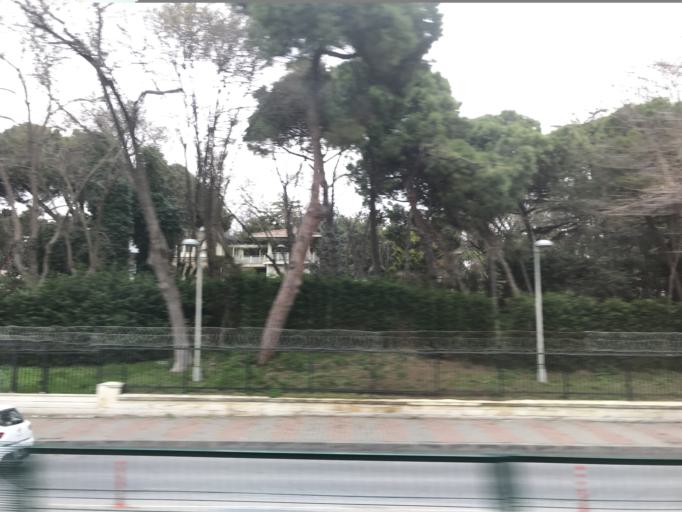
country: TR
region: Istanbul
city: Bahcelievler
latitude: 40.9734
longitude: 28.7866
